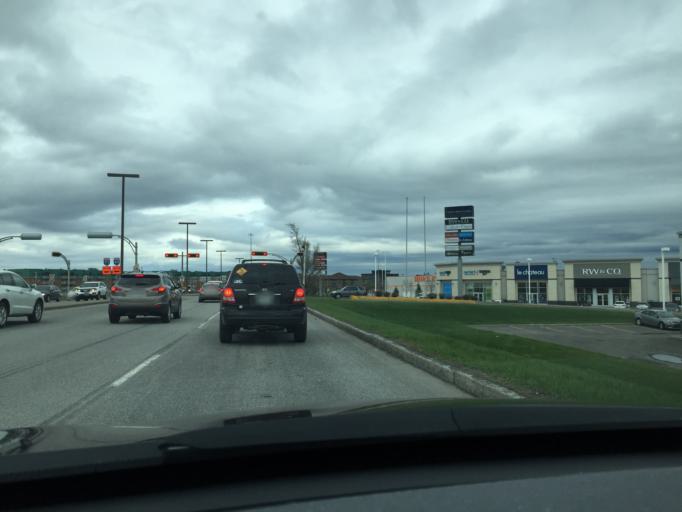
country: CA
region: Quebec
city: Quebec
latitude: 46.8447
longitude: -71.2744
